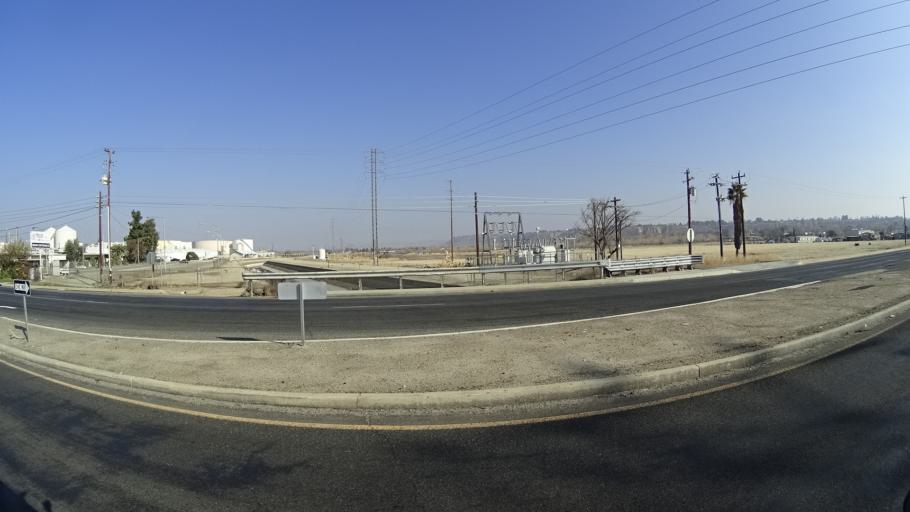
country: US
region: California
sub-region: Kern County
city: Oildale
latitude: 35.4158
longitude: -119.0130
